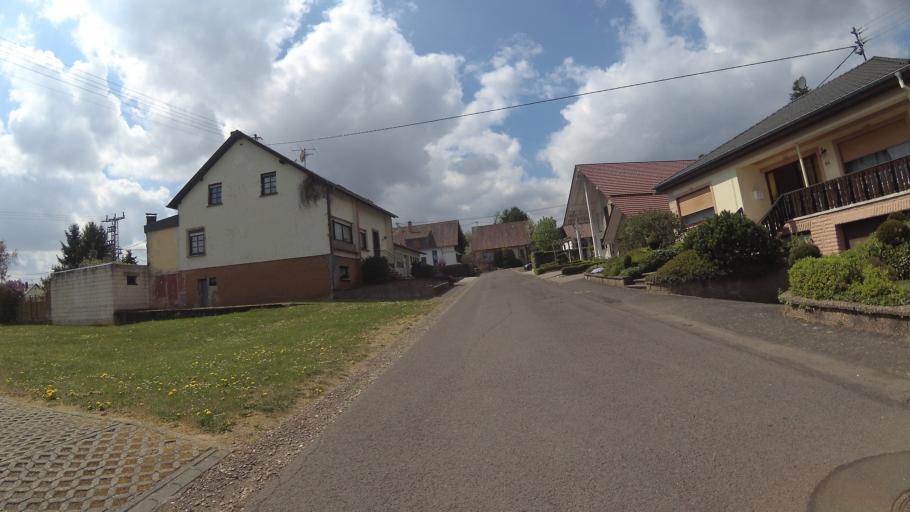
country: DE
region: Saarland
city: Weiskirchen
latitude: 49.5592
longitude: 6.8536
